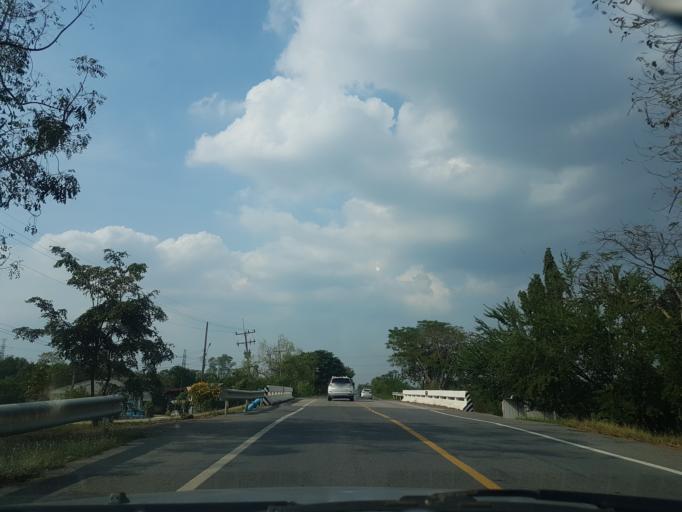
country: TH
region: Phra Nakhon Si Ayutthaya
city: Phachi
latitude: 14.4341
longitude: 100.7721
